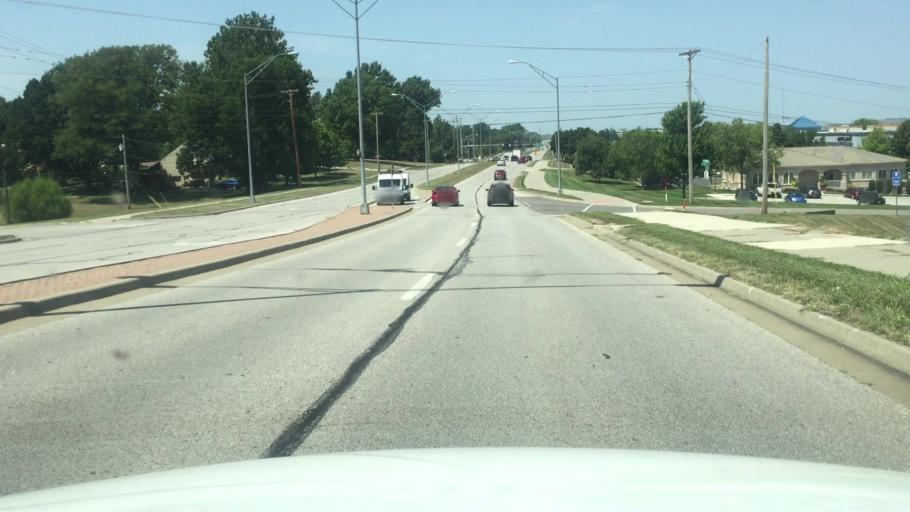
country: US
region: Missouri
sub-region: Jackson County
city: Lees Summit
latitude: 38.9251
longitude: -94.3809
